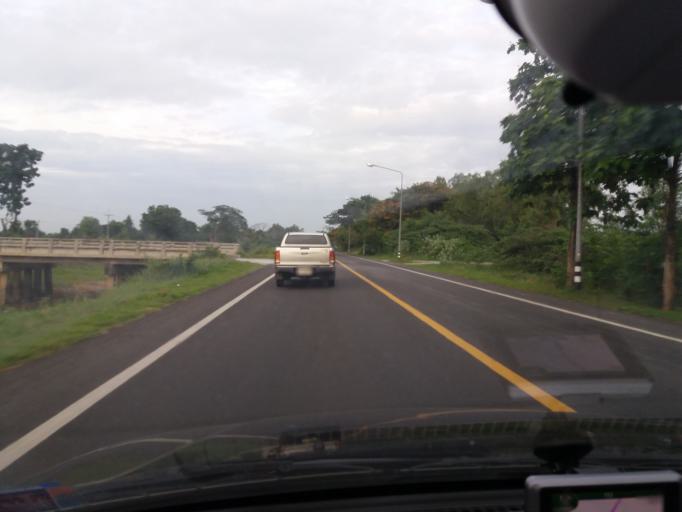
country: TH
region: Suphan Buri
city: Don Chedi
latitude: 14.5242
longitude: 99.9277
